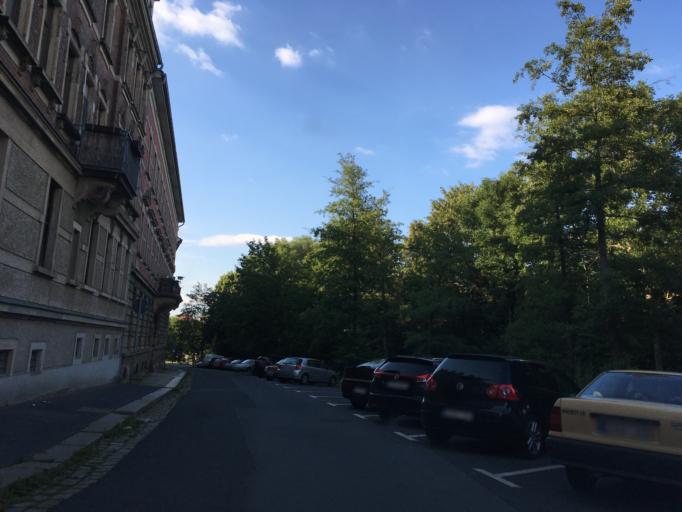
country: DE
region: Saxony
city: Radeberg
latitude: 51.1124
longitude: 13.9211
